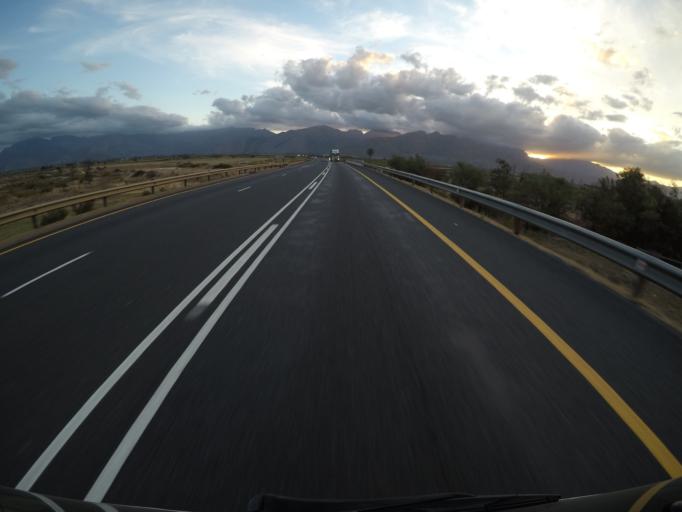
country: ZA
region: Western Cape
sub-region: Cape Winelands District Municipality
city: Worcester
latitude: -33.6348
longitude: 19.3218
